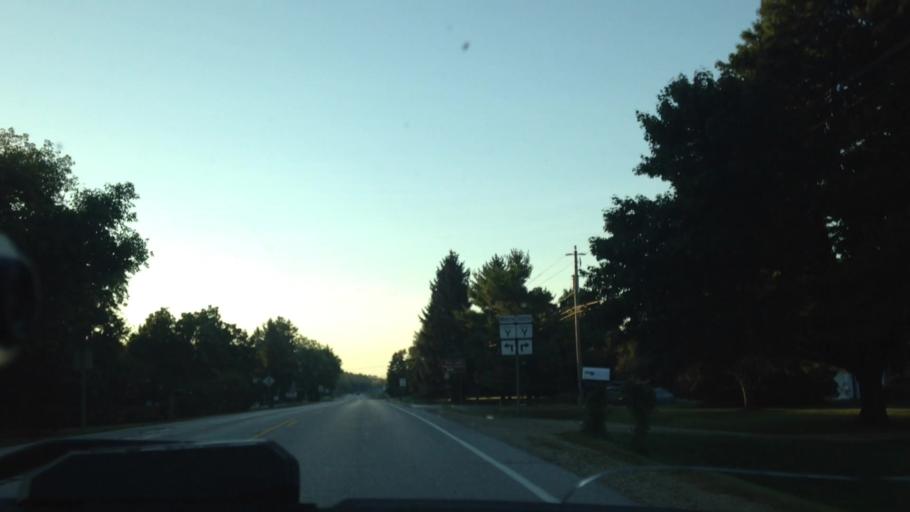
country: US
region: Wisconsin
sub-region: Washington County
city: Newburg
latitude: 43.4297
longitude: -88.0429
